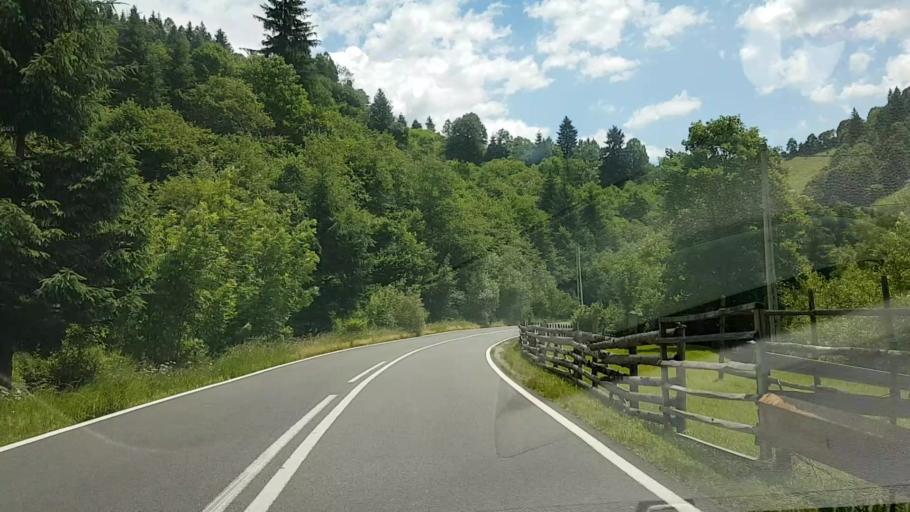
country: RO
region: Suceava
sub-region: Comuna Crucea
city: Crucea
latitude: 47.3897
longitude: 25.5803
